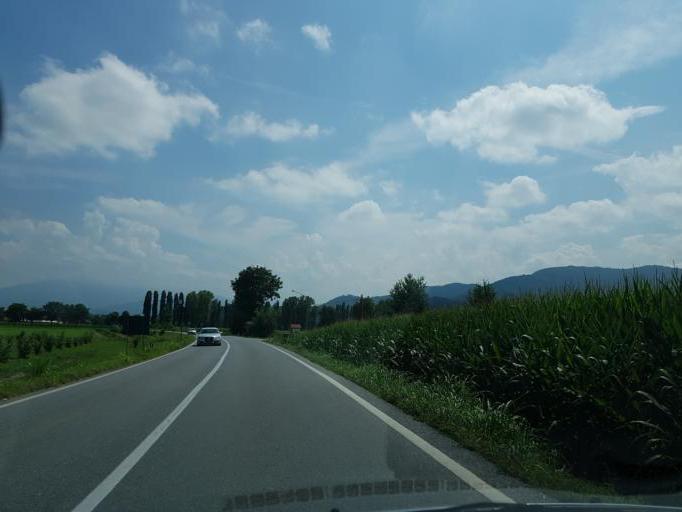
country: IT
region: Piedmont
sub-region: Provincia di Cuneo
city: Bernezzo
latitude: 44.4005
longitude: 7.4489
